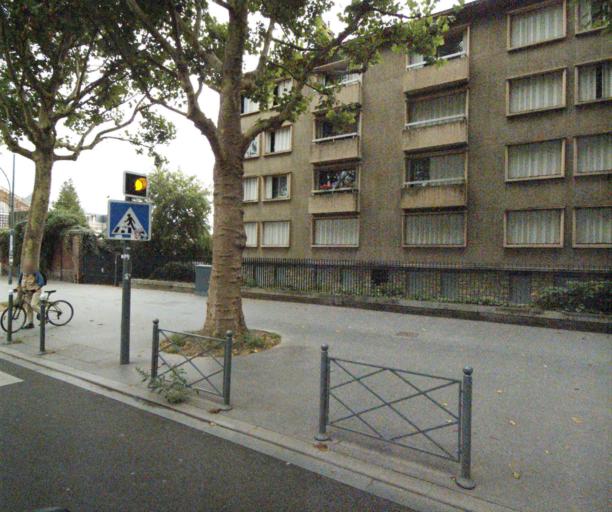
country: FR
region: Nord-Pas-de-Calais
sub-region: Departement du Nord
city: Lille
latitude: 50.6260
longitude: 3.0696
